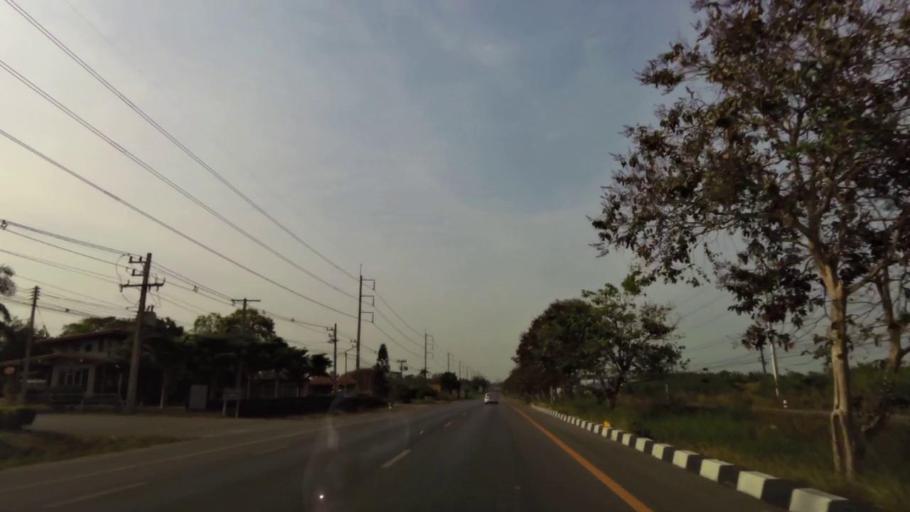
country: TH
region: Chon Buri
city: Nong Yai
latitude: 13.2174
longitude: 101.2381
